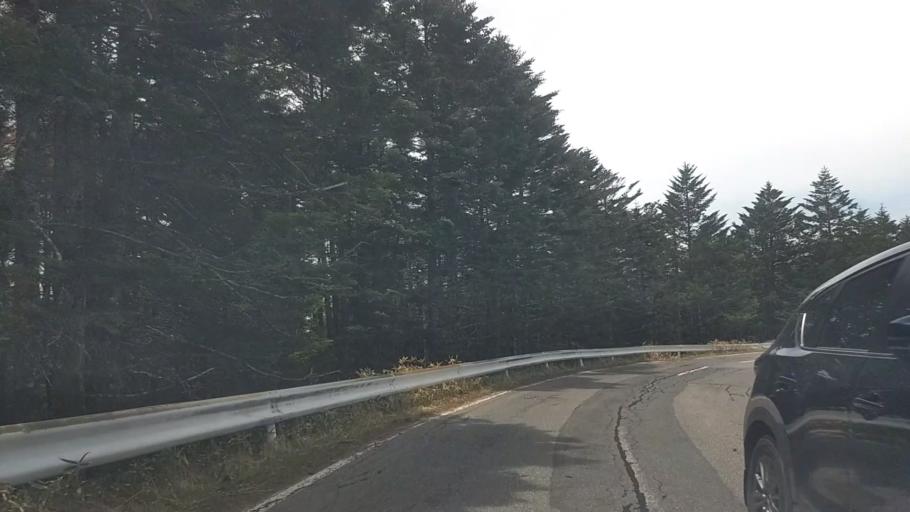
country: JP
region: Nagano
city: Chino
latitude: 36.0559
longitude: 138.3213
